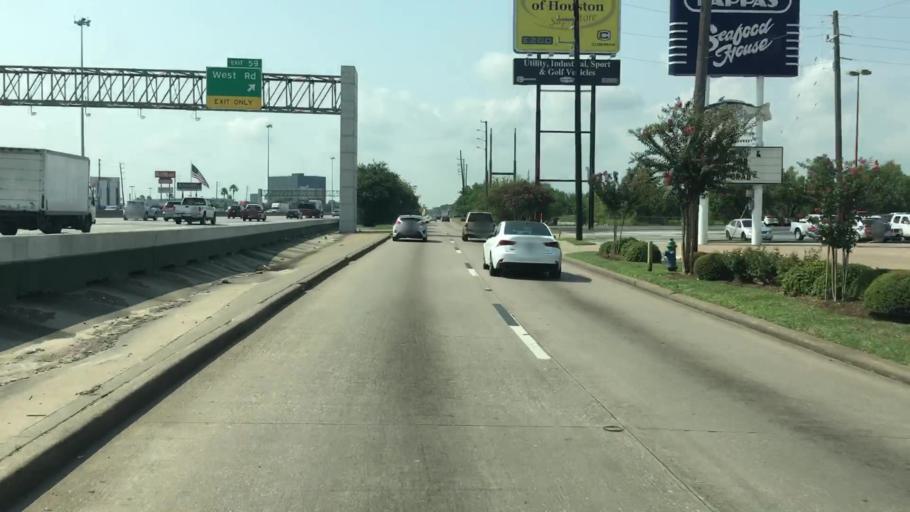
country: US
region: Texas
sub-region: Harris County
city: Aldine
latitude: 29.9300
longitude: -95.4122
